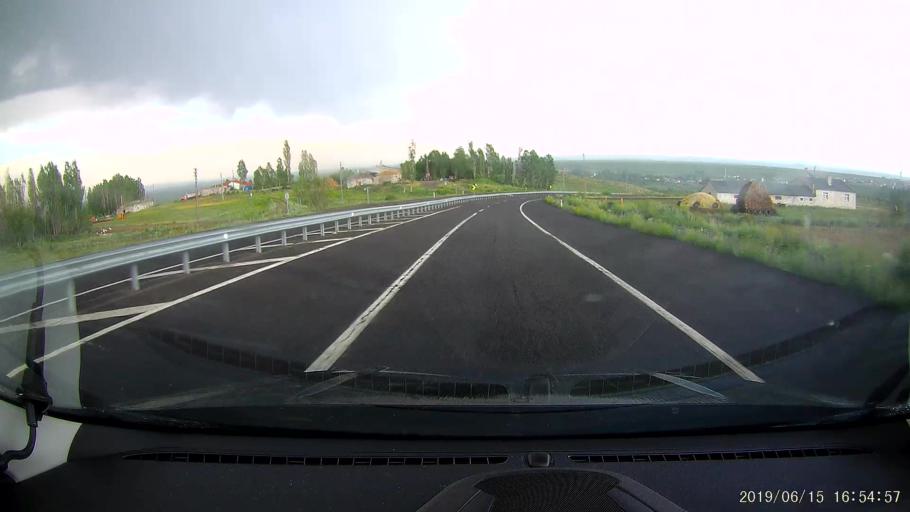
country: TR
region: Kars
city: Susuz
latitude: 40.7875
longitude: 43.1352
